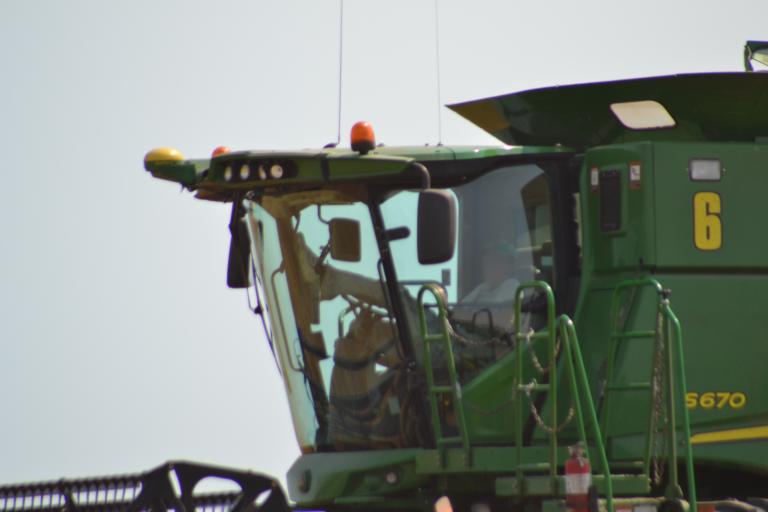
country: US
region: North Dakota
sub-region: Adams County
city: Hettinger
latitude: 45.9064
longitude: -102.9365
